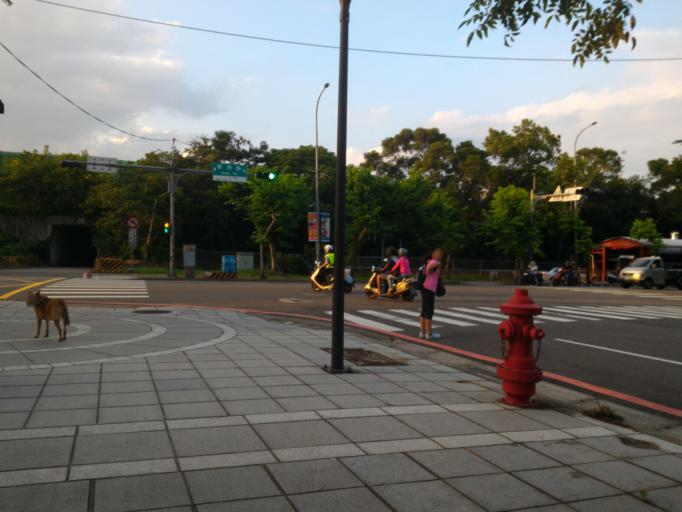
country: TW
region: Taiwan
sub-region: Taoyuan
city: Taoyuan
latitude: 24.9507
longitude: 121.3812
